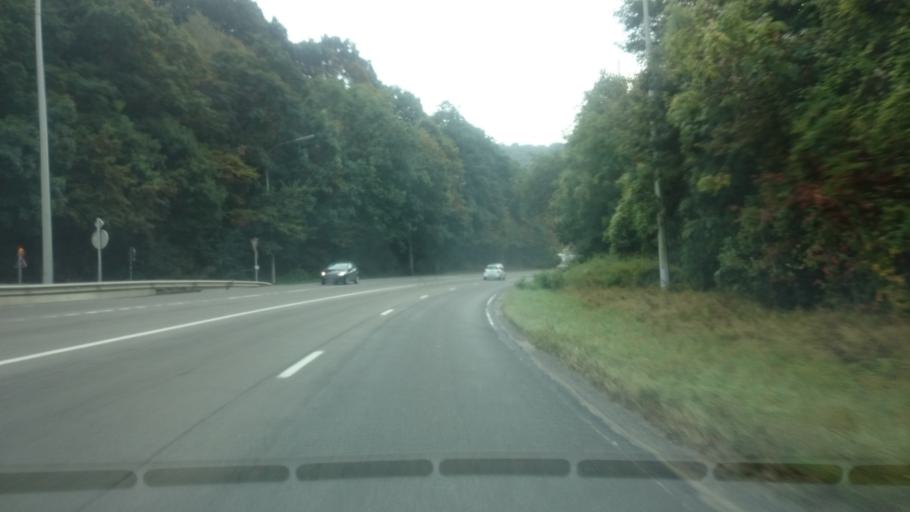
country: BE
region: Wallonia
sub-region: Province de Namur
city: Namur
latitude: 50.4504
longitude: 4.8345
